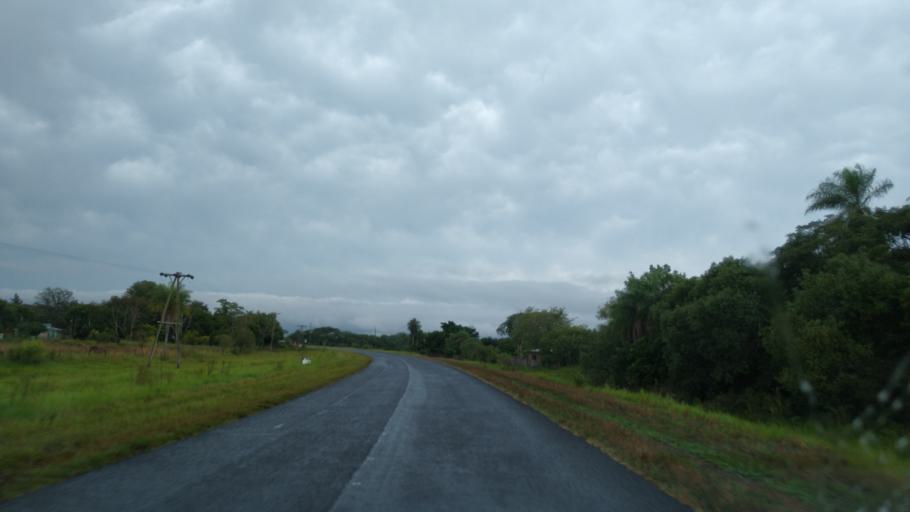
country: AR
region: Corrientes
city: Loreto
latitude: -27.7736
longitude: -57.2695
